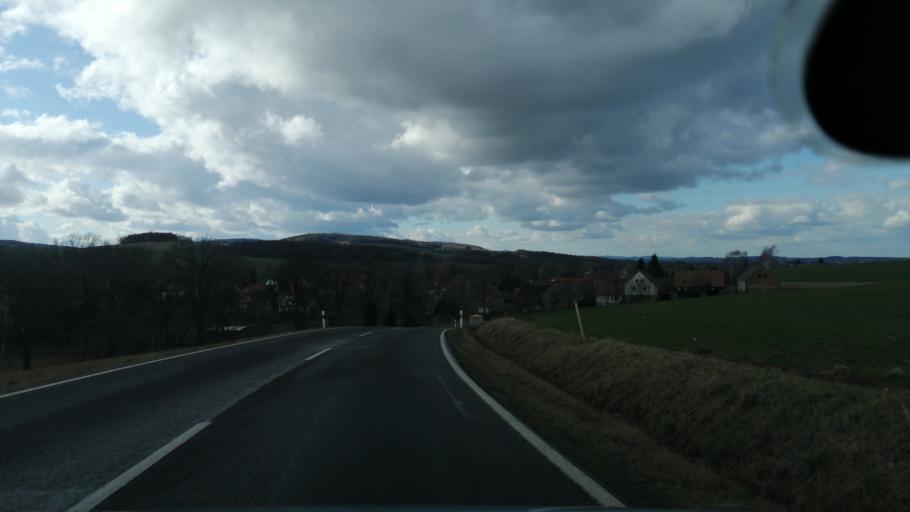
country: DE
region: Saxony
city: Hochkirch
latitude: 51.1436
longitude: 14.5427
